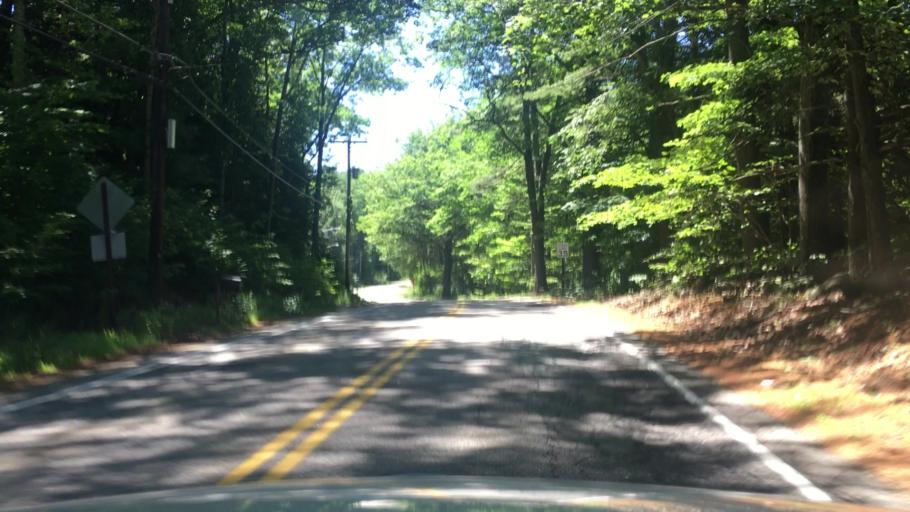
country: US
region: New Hampshire
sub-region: Merrimack County
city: Boscawen
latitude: 43.2483
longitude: -71.6192
